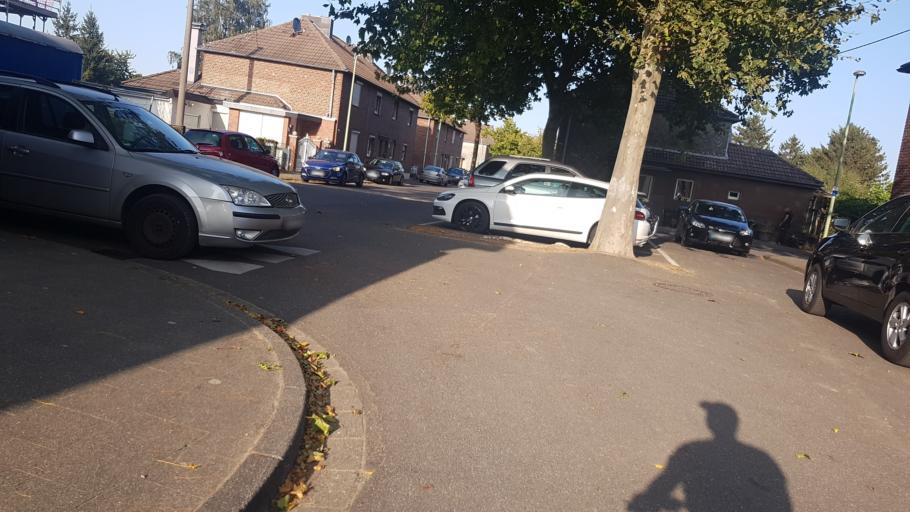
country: DE
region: North Rhine-Westphalia
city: Baesweiler
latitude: 50.9012
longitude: 6.1758
